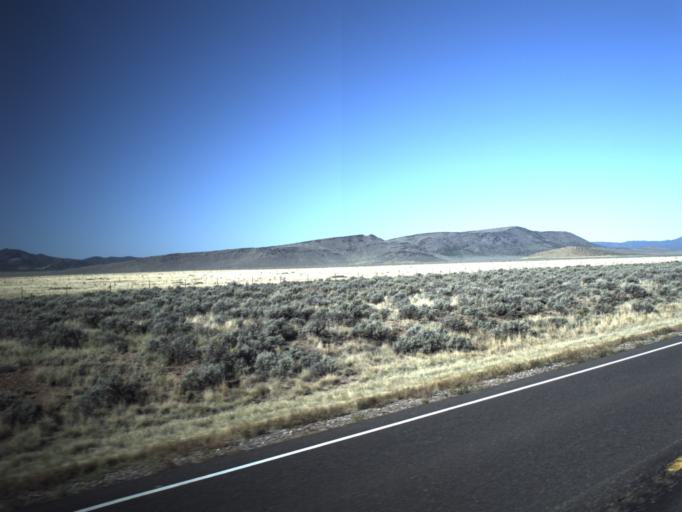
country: US
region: Utah
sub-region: Washington County
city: Enterprise
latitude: 37.7683
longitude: -113.8229
